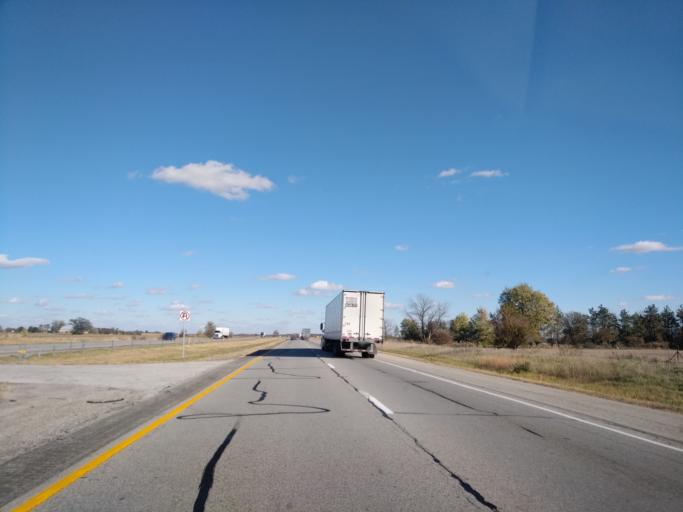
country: US
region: Indiana
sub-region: Henry County
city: Knightstown
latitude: 39.8259
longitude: -85.6387
